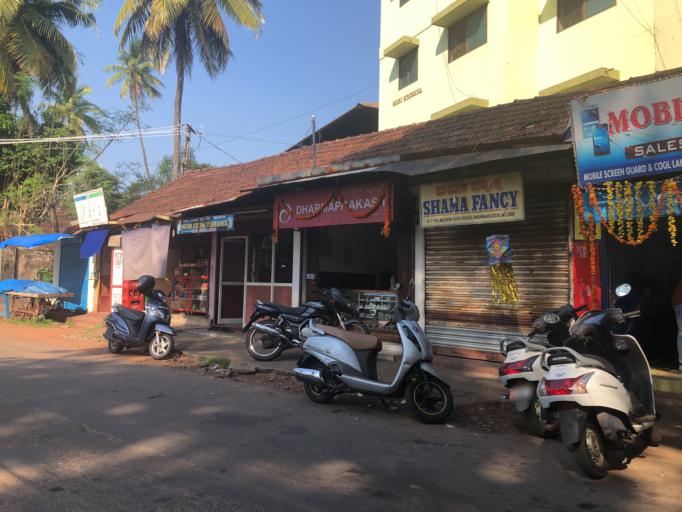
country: IN
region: Karnataka
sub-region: Dakshina Kannada
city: Mangalore
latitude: 12.8846
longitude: 74.8329
